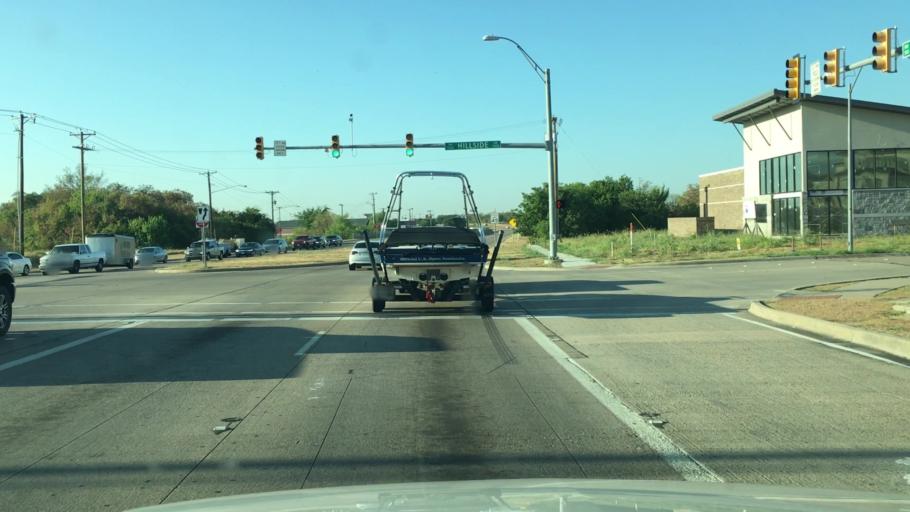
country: US
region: Texas
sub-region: Johnson County
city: Burleson
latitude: 32.5303
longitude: -97.3529
